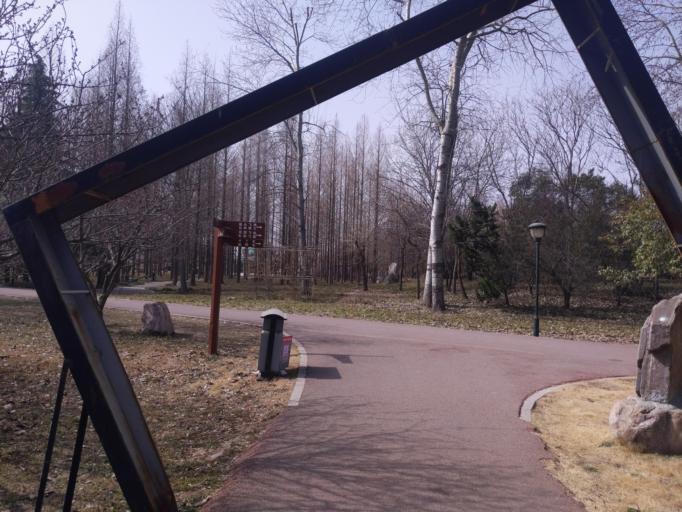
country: CN
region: Henan Sheng
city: Puyang
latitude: 35.7762
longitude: 114.9627
